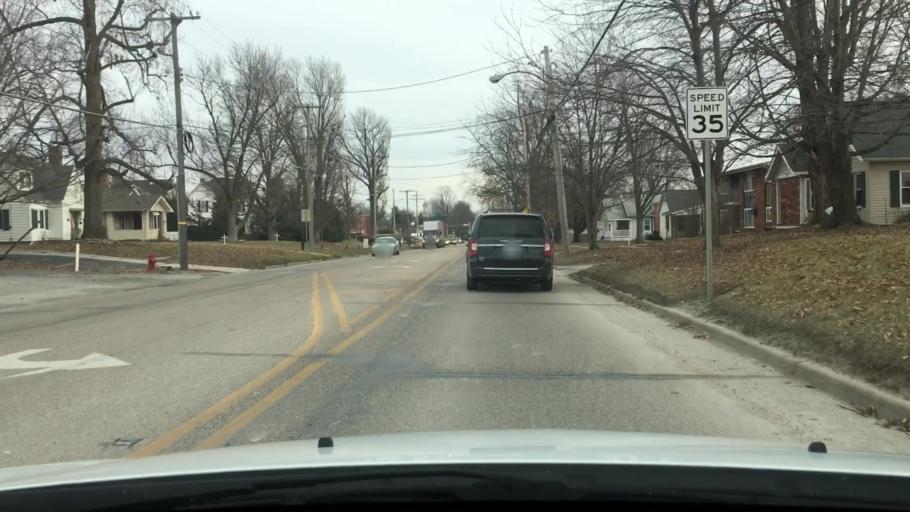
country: US
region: Illinois
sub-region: Pike County
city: Pittsfield
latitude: 39.6068
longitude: -90.8180
